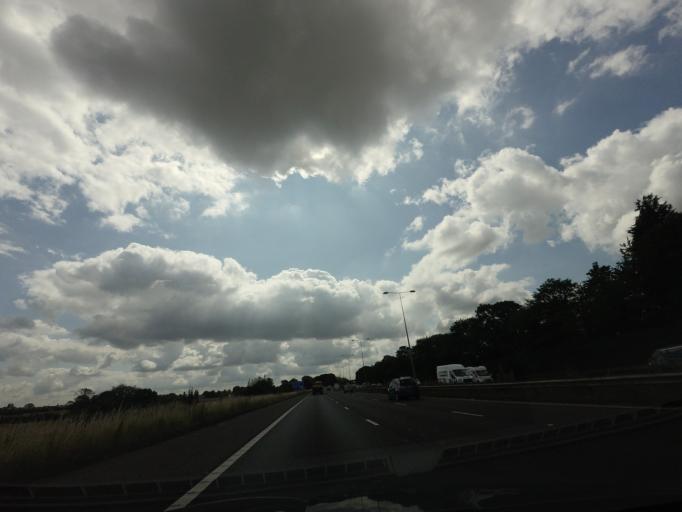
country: GB
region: England
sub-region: Borough of Wigan
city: Shevington
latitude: 53.5441
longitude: -2.6975
